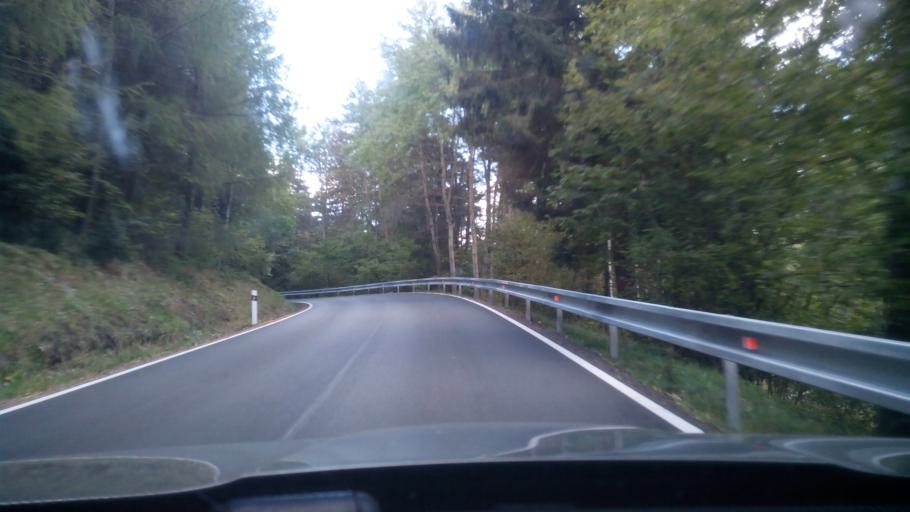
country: CZ
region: Plzensky
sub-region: Okres Klatovy
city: Kasperske Hory
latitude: 49.1413
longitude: 13.6017
